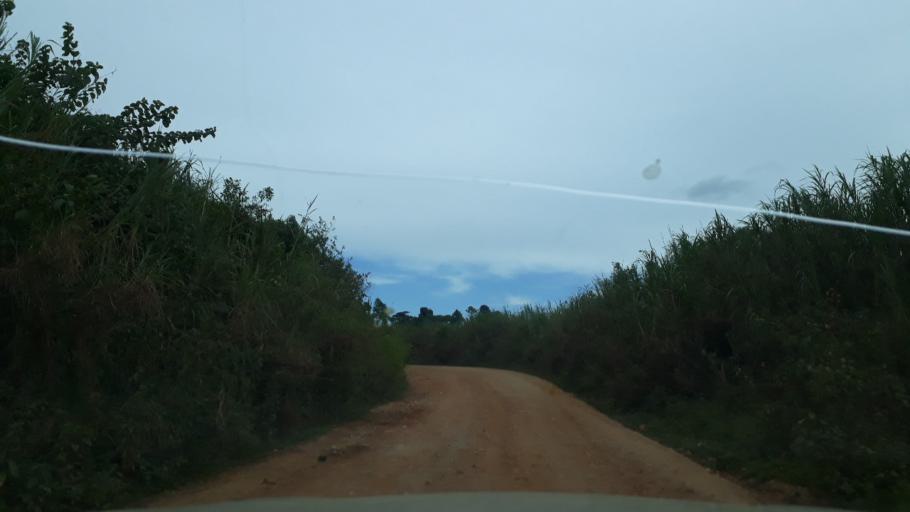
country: CD
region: Eastern Province
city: Bunia
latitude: 1.9272
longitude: 30.5123
